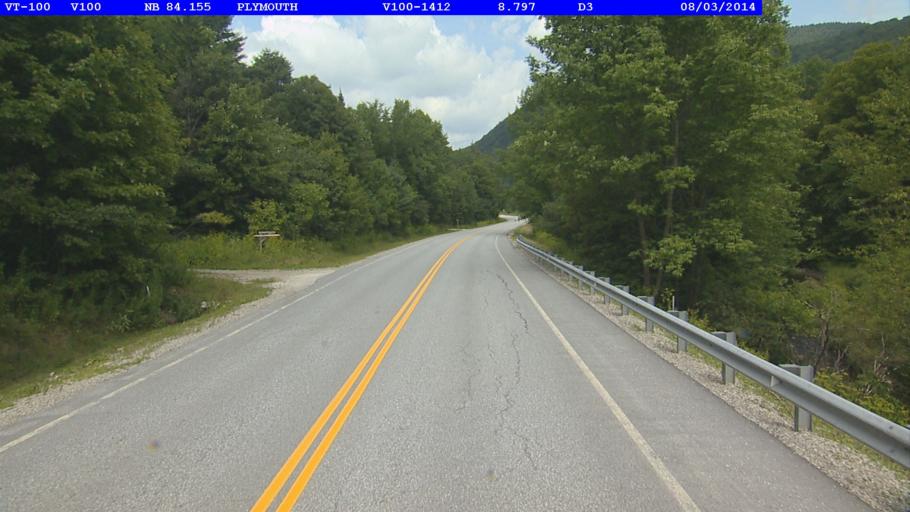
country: US
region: Vermont
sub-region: Rutland County
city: Rutland
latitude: 43.5749
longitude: -72.7613
